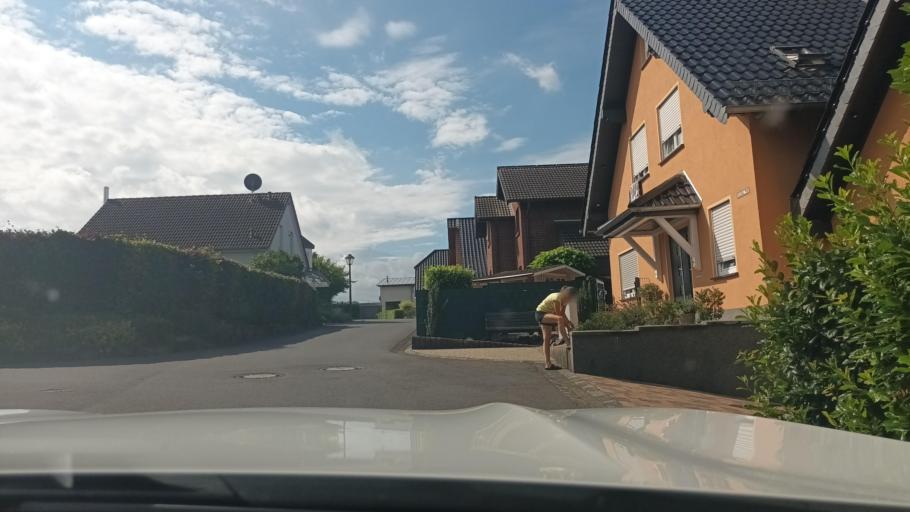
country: DE
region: North Rhine-Westphalia
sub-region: Regierungsbezirk Koln
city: Hennef
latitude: 50.7615
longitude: 7.3121
